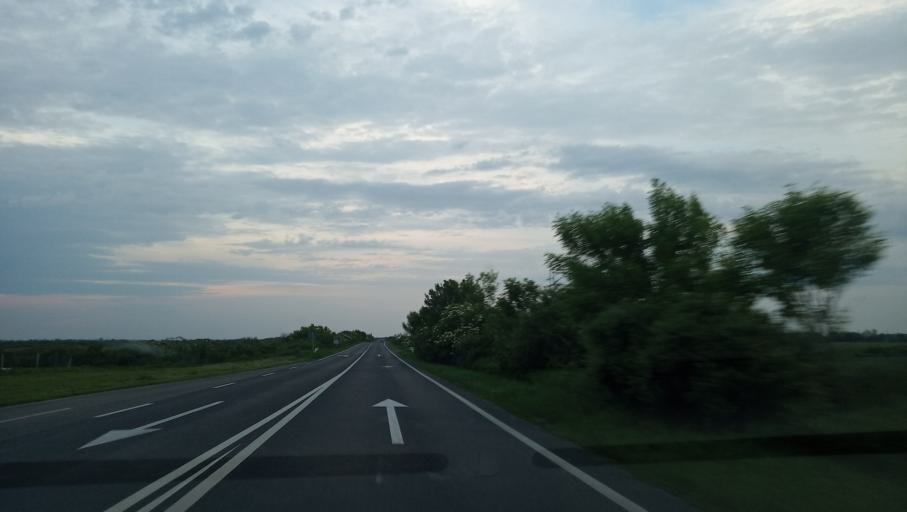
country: RO
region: Timis
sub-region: Comuna Voiteg
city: Voiteg
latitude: 45.4858
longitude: 21.2340
